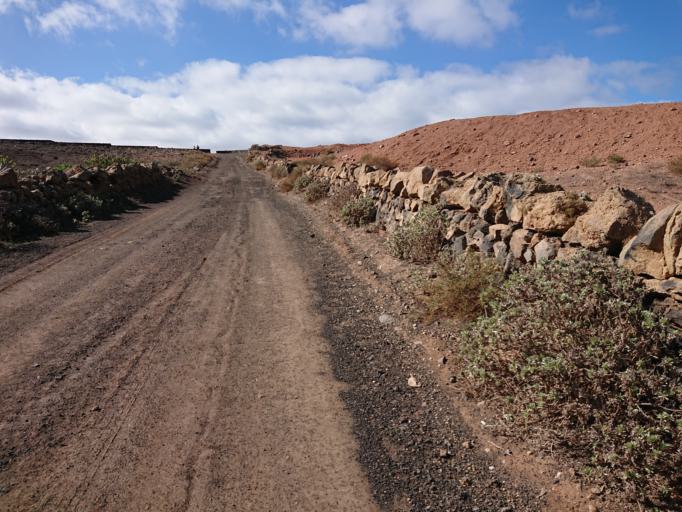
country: ES
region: Canary Islands
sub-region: Provincia de Las Palmas
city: Haria
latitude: 29.1455
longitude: -13.5182
